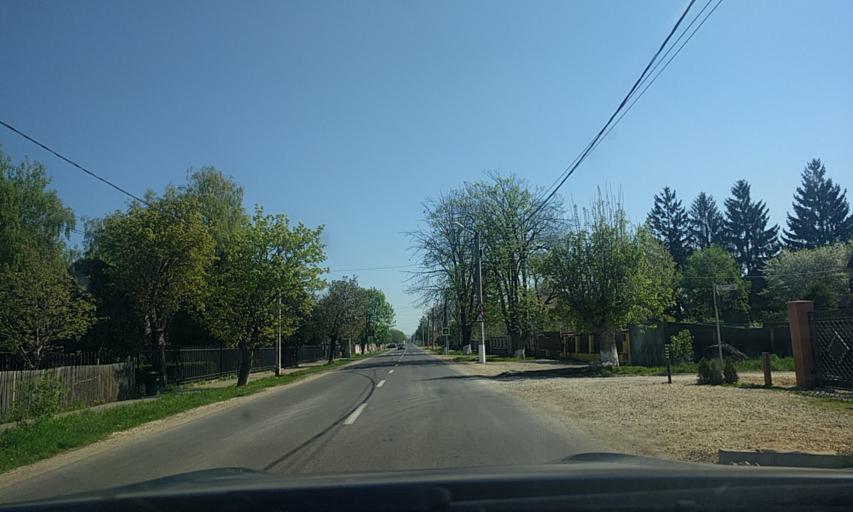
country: RO
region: Brasov
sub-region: Comuna Ghimbav
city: Ghimbav
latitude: 45.6985
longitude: 25.5588
